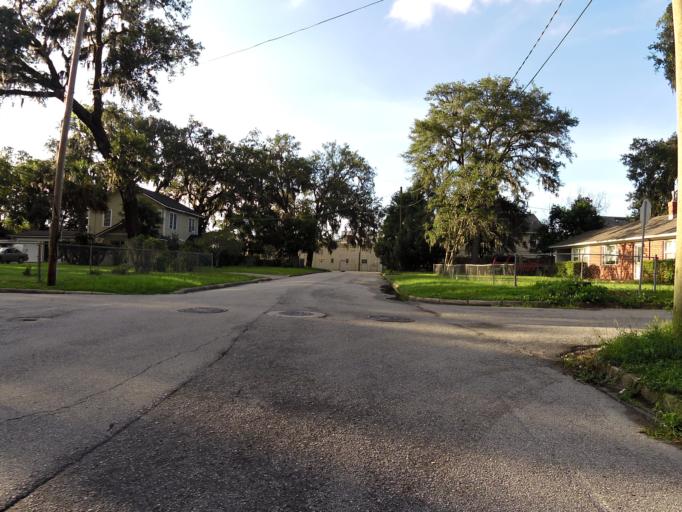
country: US
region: Florida
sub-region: Duval County
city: Jacksonville
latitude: 30.3001
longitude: -81.6281
